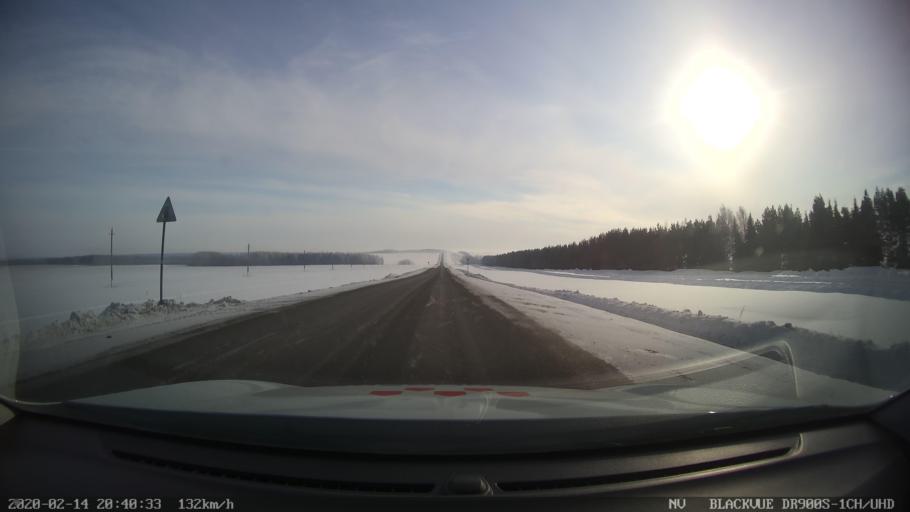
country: RU
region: Tatarstan
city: Kuybyshevskiy Zaton
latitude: 55.3391
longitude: 49.0929
